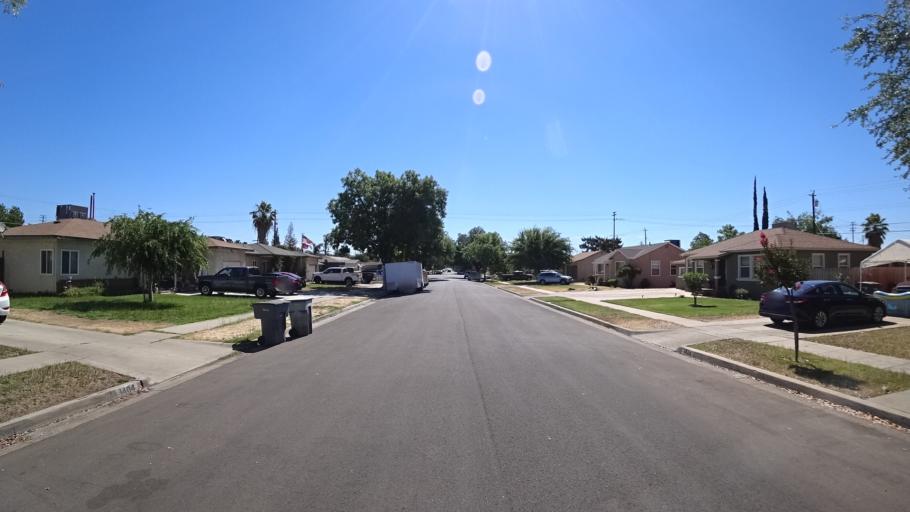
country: US
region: California
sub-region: Fresno County
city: Fresno
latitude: 36.7829
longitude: -119.8278
